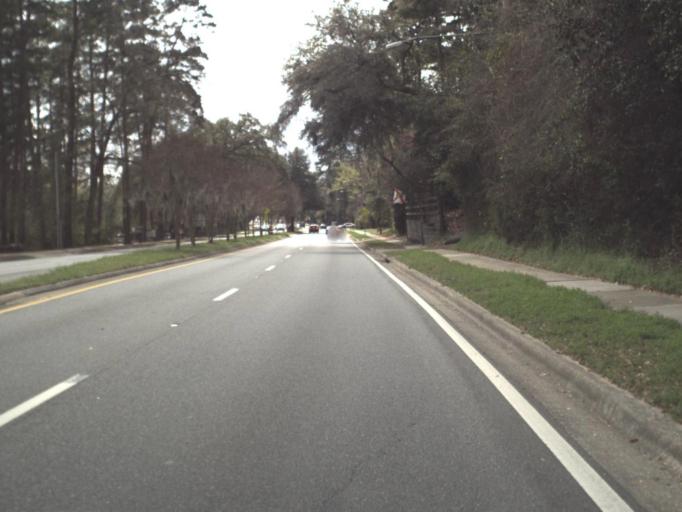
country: US
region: Florida
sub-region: Leon County
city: Tallahassee
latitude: 30.4743
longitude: -84.2642
